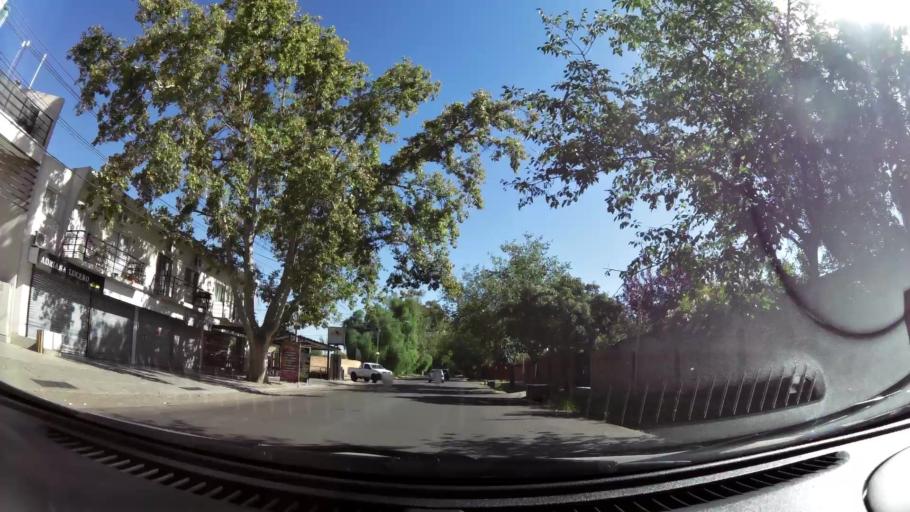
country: AR
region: Mendoza
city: Villa Nueva
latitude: -32.9101
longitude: -68.7920
